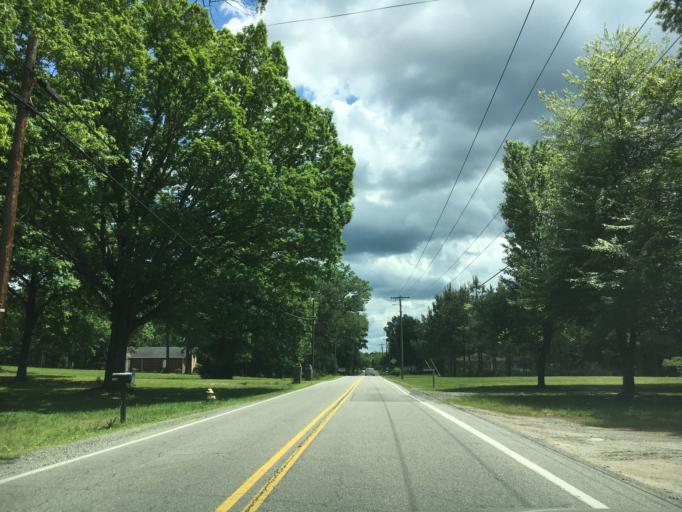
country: US
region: Virginia
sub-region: Halifax County
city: South Boston
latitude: 36.7037
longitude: -78.9256
